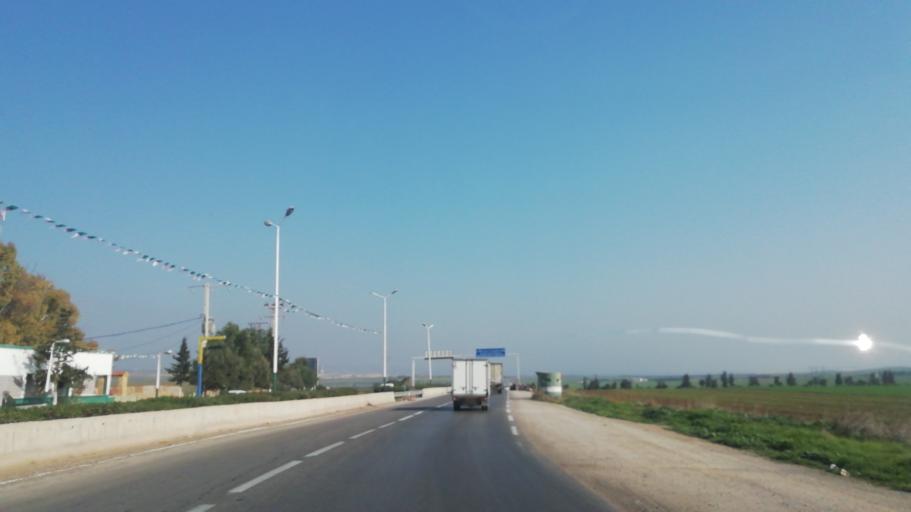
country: DZ
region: Ain Temouchent
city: El Amria
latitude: 35.5459
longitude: -0.9640
